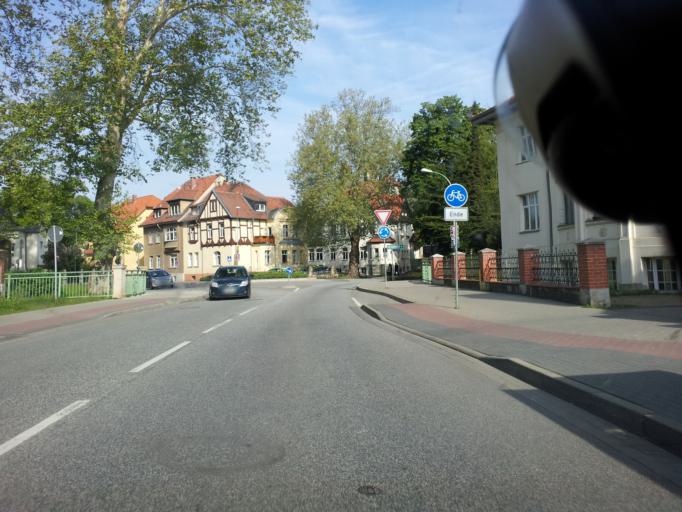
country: DE
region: Saxony-Anhalt
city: Quedlinburg
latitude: 51.7840
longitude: 11.1405
